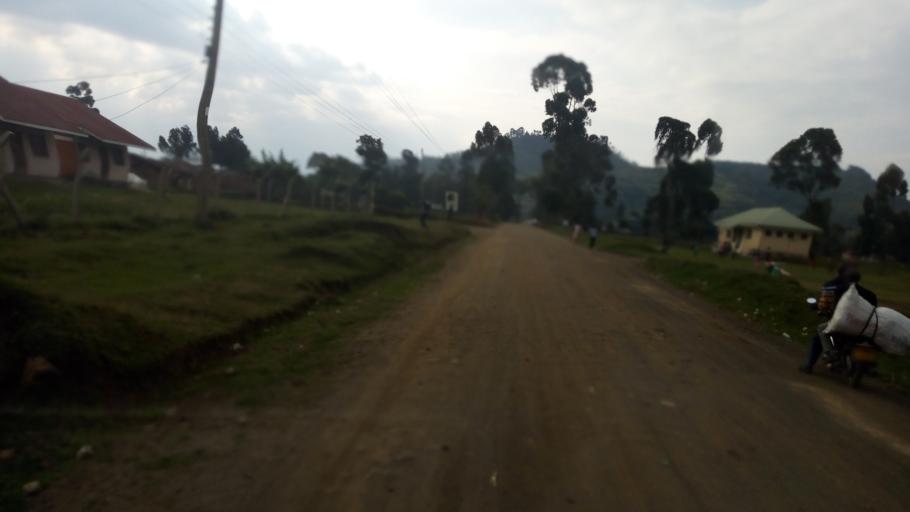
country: UG
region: Western Region
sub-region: Kisoro District
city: Kisoro
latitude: -1.2868
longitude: 29.6902
